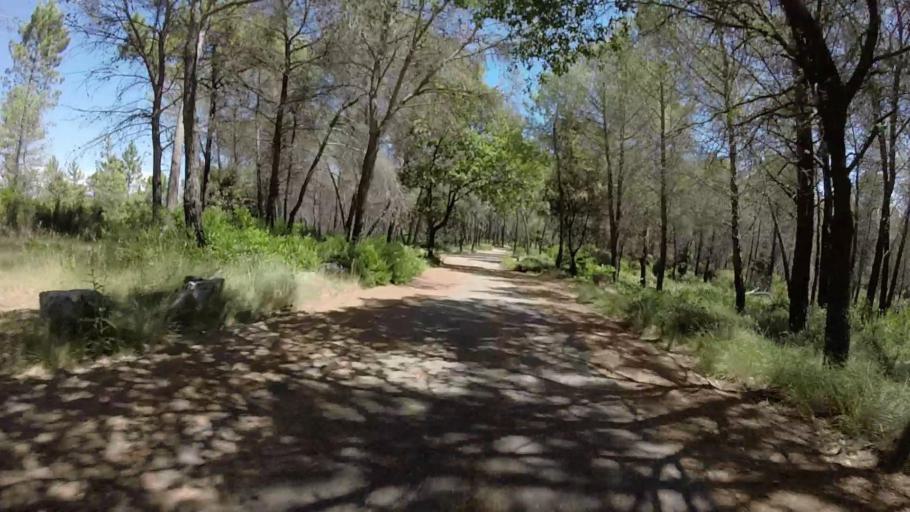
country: FR
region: Provence-Alpes-Cote d'Azur
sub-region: Departement des Alpes-Maritimes
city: Vallauris
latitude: 43.6087
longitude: 7.0469
